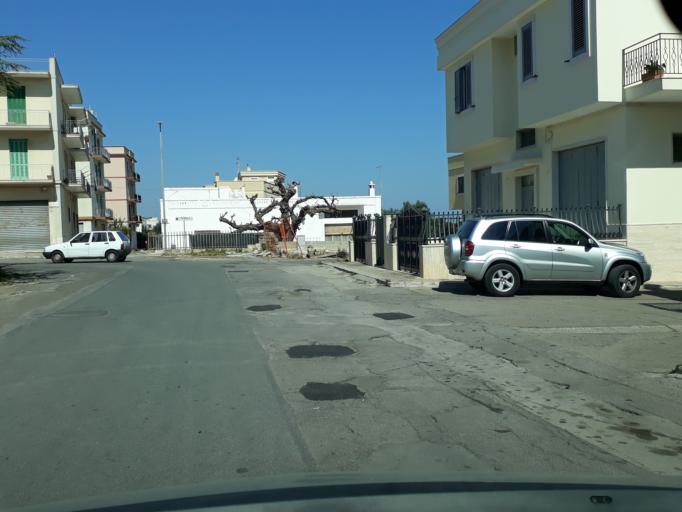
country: IT
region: Apulia
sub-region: Provincia di Brindisi
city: Fasano
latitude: 40.8395
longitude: 17.3625
